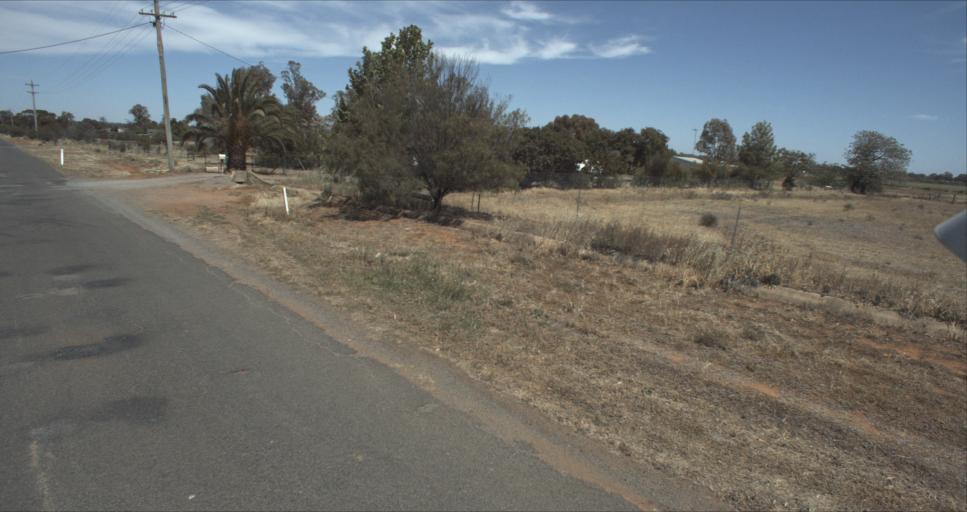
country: AU
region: New South Wales
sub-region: Leeton
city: Leeton
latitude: -34.5959
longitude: 146.4279
